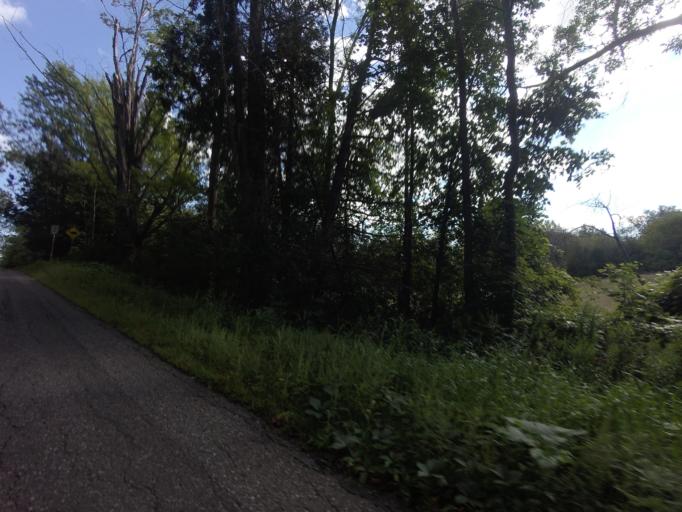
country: CA
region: Ontario
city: Orangeville
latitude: 43.8197
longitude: -79.9895
